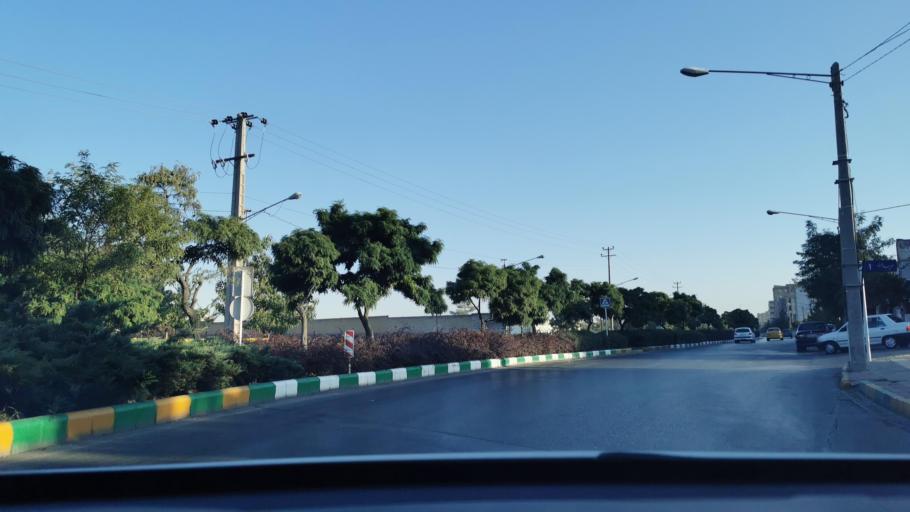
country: IR
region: Razavi Khorasan
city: Mashhad
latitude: 36.3458
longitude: 59.5142
